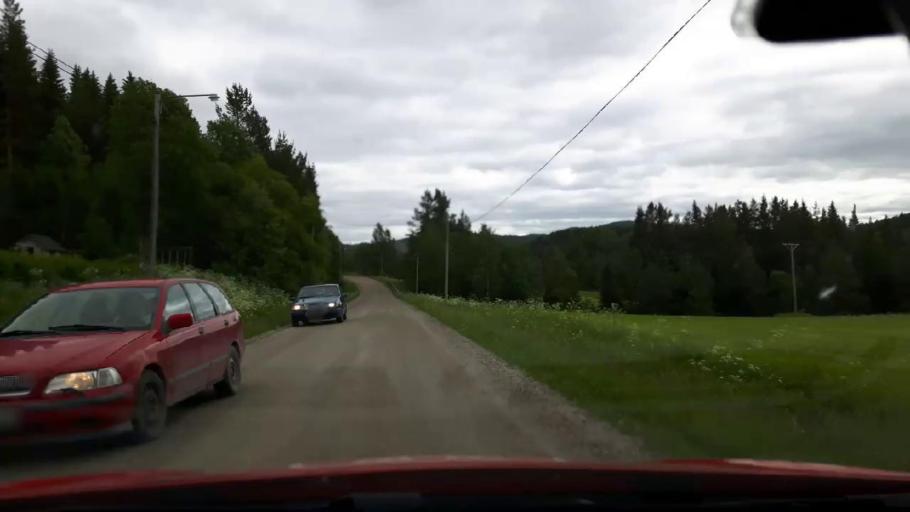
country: SE
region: Jaemtland
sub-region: Ragunda Kommun
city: Hammarstrand
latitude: 63.1705
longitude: 16.2045
